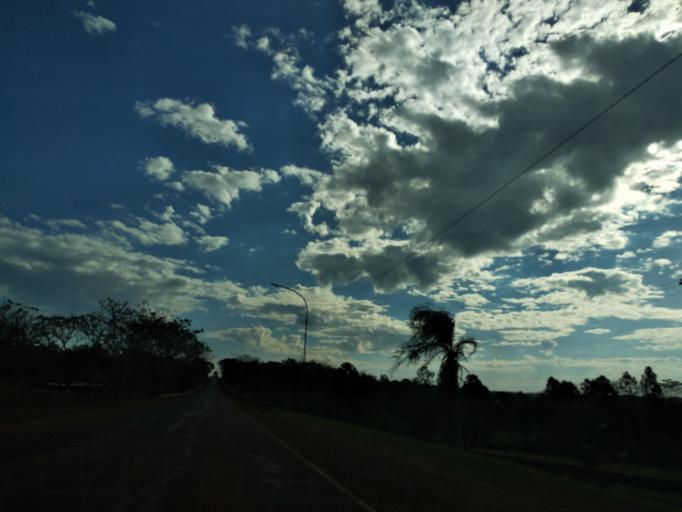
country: AR
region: Misiones
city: Jardin America
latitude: -27.0364
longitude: -55.2195
